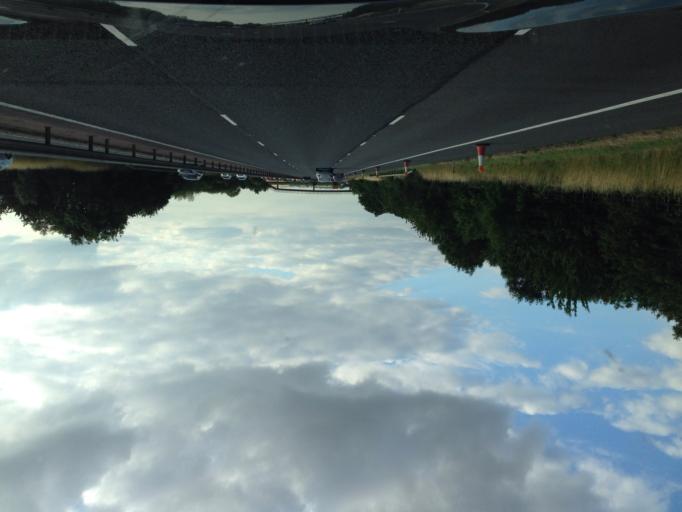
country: GB
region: England
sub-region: Oxfordshire
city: Wheatley
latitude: 51.7779
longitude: -1.0971
